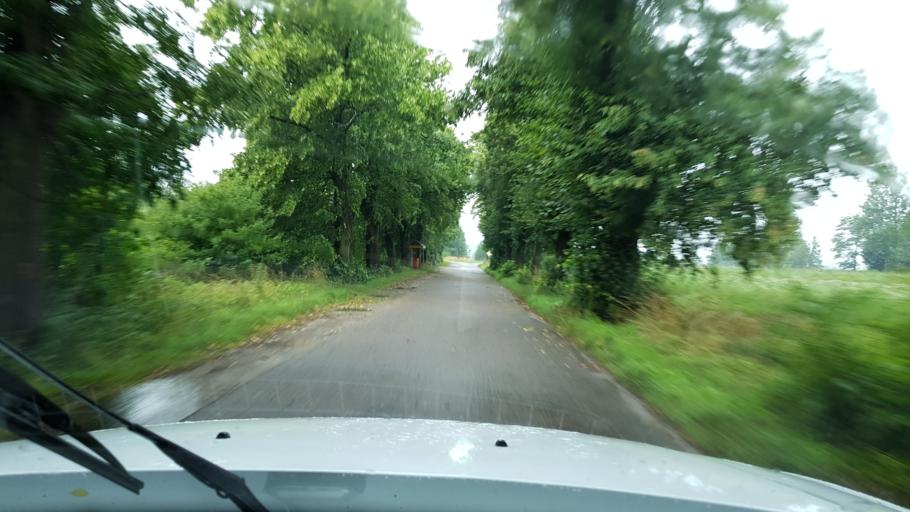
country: PL
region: West Pomeranian Voivodeship
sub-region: Powiat kolobrzeski
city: Ustronie Morskie
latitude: 54.2139
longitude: 15.8639
